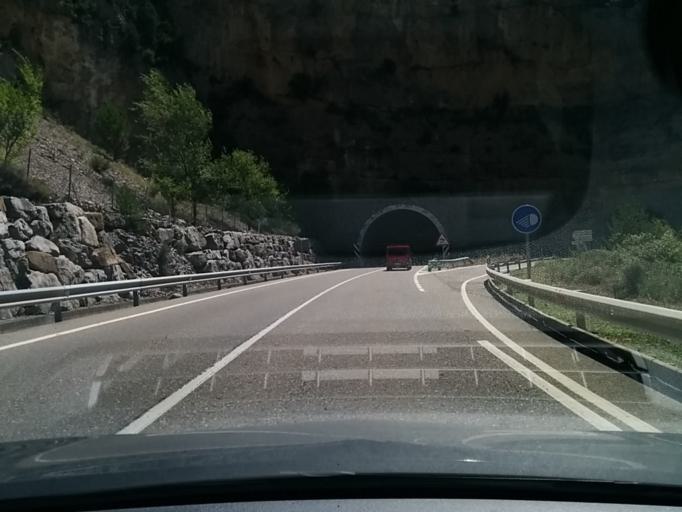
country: ES
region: Aragon
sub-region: Provincia de Huesca
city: Boltana
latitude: 42.4676
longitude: 0.0208
